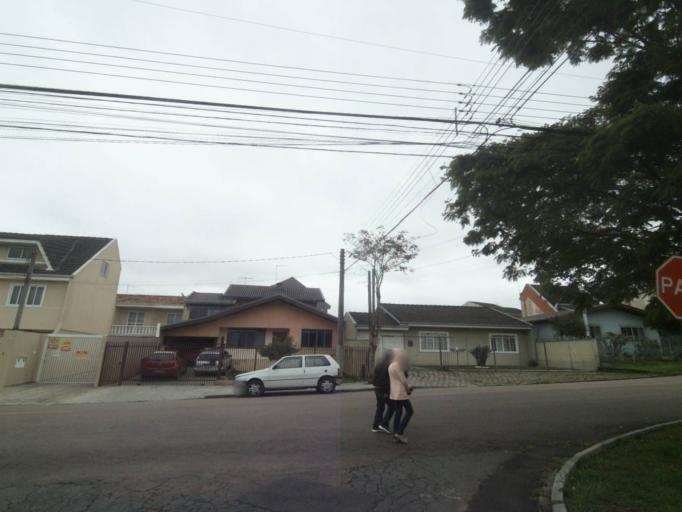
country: BR
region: Parana
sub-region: Curitiba
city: Curitiba
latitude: -25.4979
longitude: -49.2814
